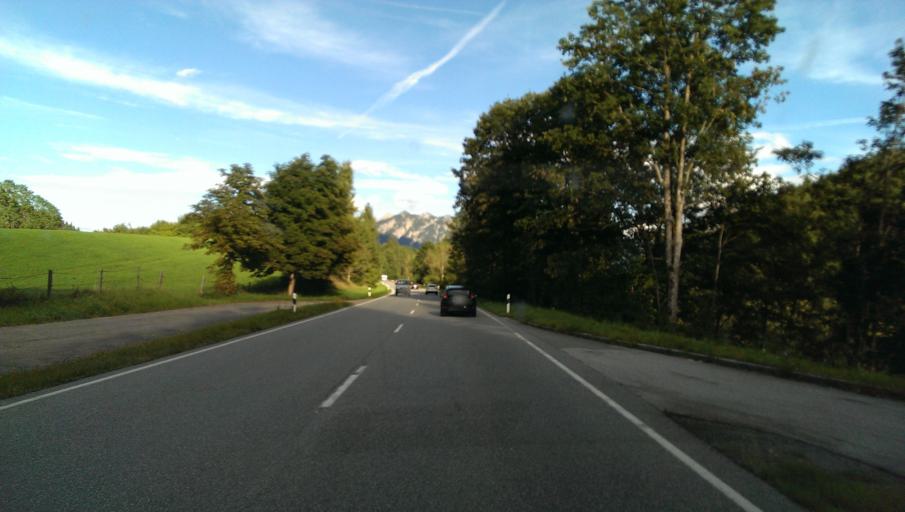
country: DE
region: Bavaria
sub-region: Upper Bavaria
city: Mittenwald
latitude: 47.4893
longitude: 11.2107
